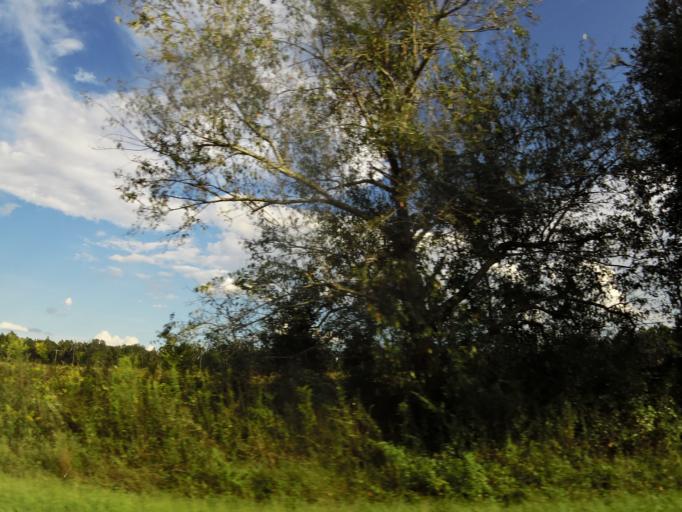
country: US
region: Georgia
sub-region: Lowndes County
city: Remerton
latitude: 30.7935
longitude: -83.3919
